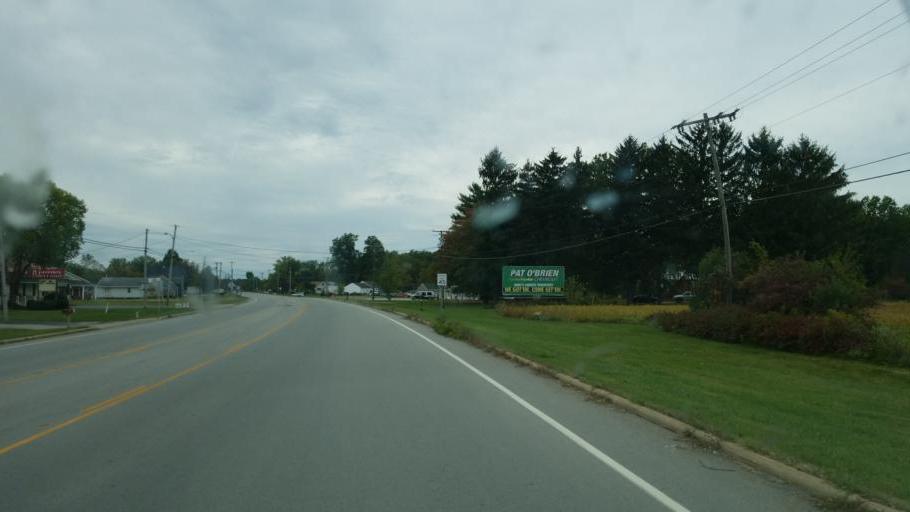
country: US
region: Ohio
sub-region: Lorain County
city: Amherst
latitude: 41.3664
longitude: -82.2124
